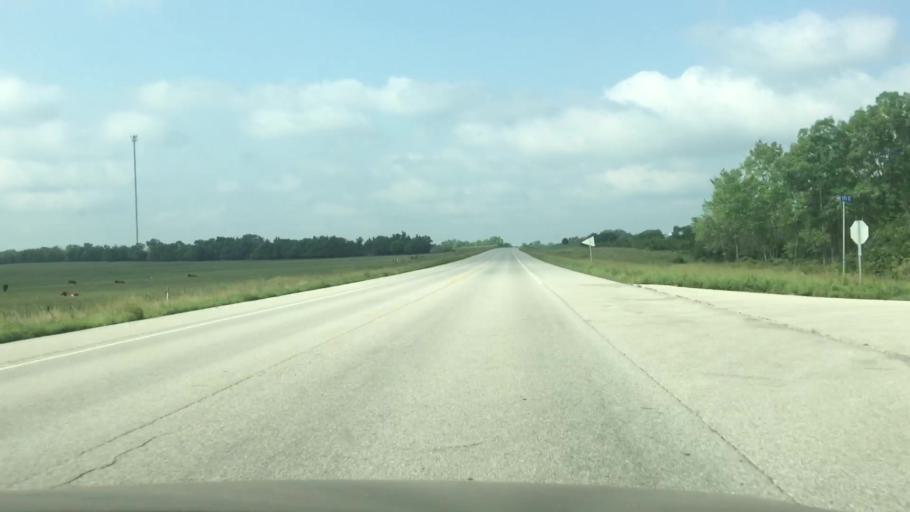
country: US
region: Kansas
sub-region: Miami County
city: Osawatomie
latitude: 38.4114
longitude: -95.0488
